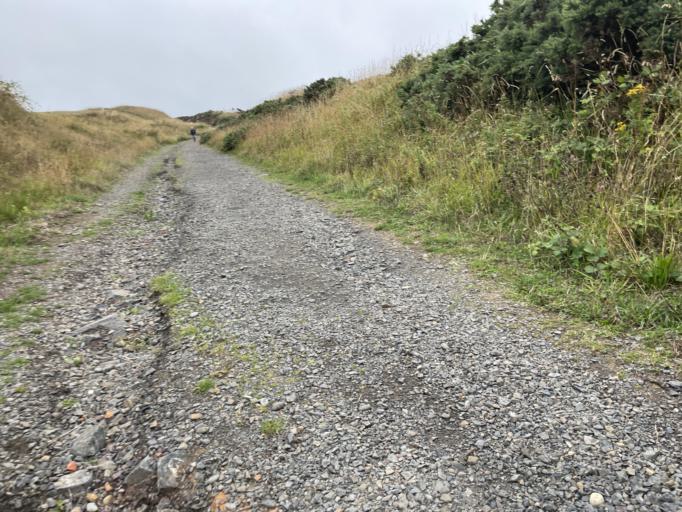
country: GB
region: Scotland
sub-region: Dumfries and Galloway
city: Stranraer
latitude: 54.8398
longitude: -5.1145
